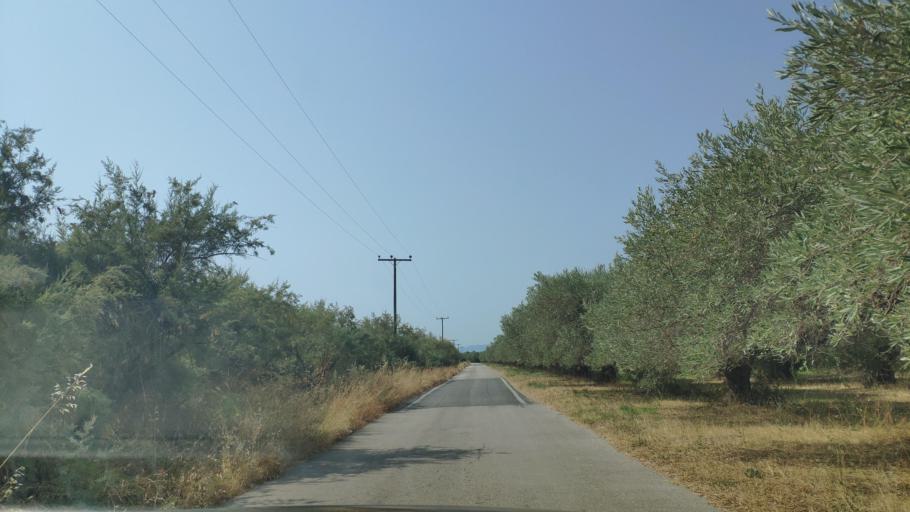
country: GR
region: West Greece
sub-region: Nomos Aitolias kai Akarnanias
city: Menidi
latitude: 39.0477
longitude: 21.0722
